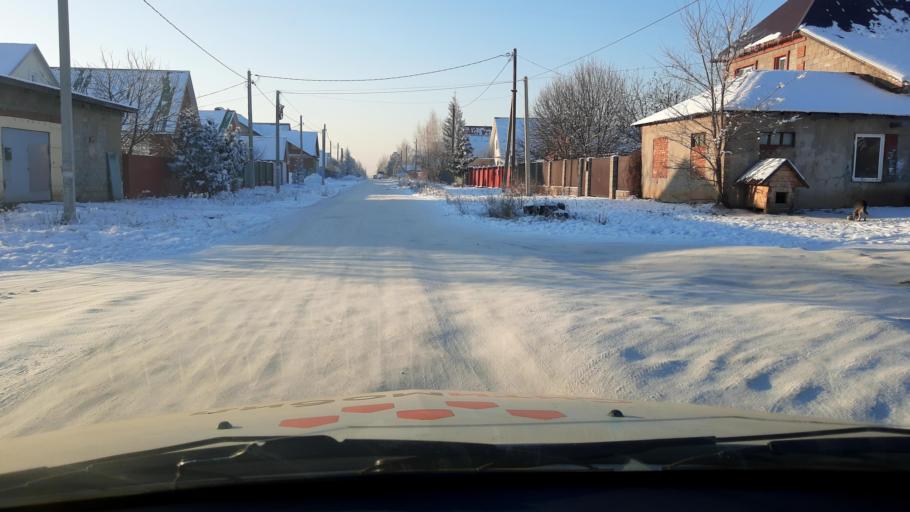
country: RU
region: Bashkortostan
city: Iglino
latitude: 54.7864
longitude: 56.2452
